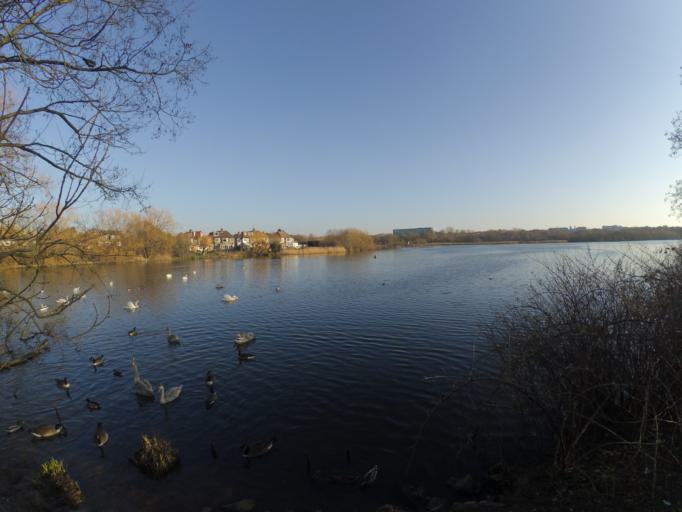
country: GB
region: England
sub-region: Greater London
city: Hendon
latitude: 51.5746
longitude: -0.2431
